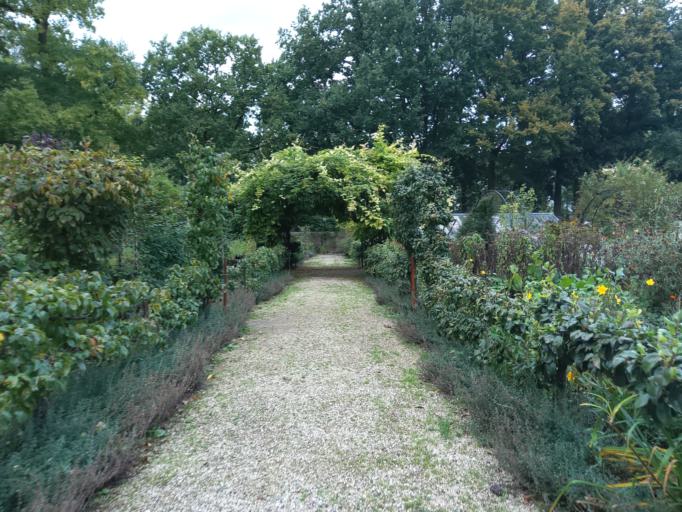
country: NL
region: Gelderland
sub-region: Gemeente Neerijnen
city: Neerijnen
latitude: 51.8319
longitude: 5.2791
